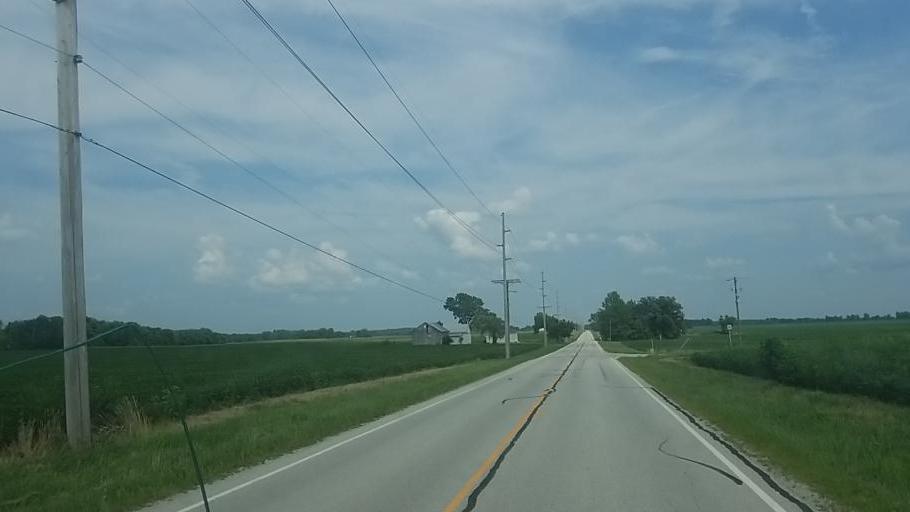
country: US
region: Ohio
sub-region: Hardin County
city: Forest
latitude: 40.7820
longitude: -83.5582
